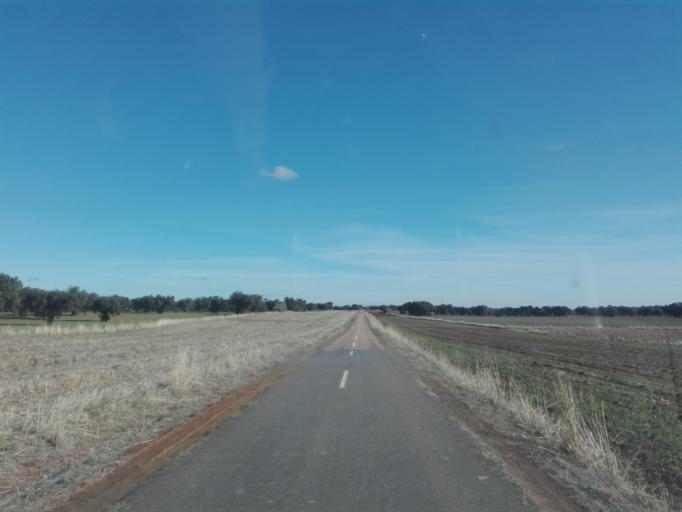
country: ES
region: Extremadura
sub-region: Provincia de Badajoz
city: Valencia de las Torres
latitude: 38.3298
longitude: -5.9410
